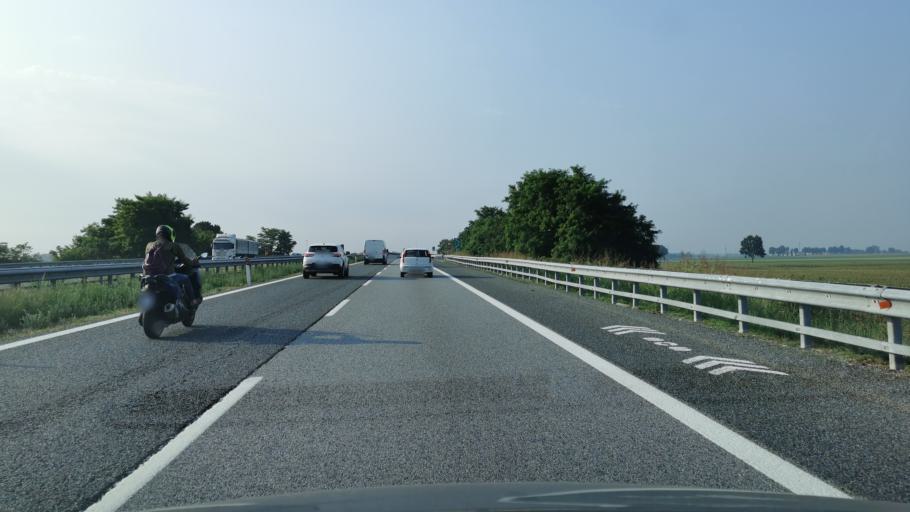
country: IT
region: Piedmont
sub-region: Provincia di Torino
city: Villastellone
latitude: 44.9091
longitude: 7.7407
